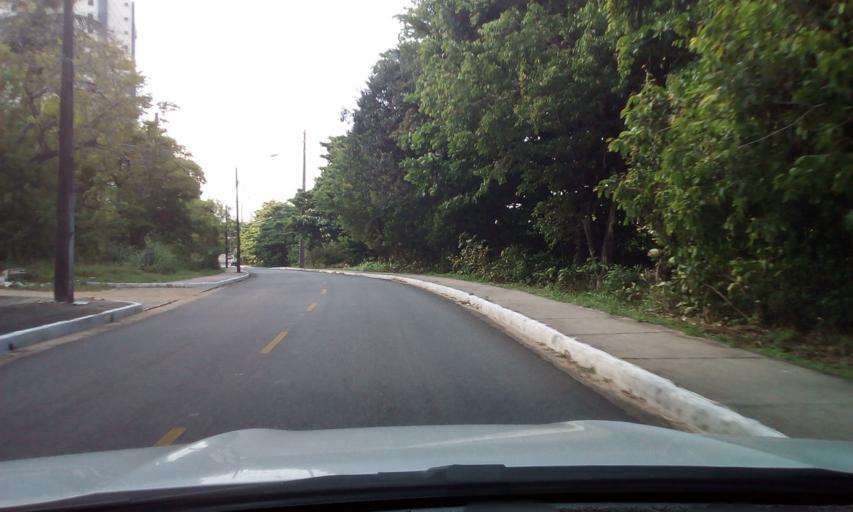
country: BR
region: Paraiba
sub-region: Joao Pessoa
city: Joao Pessoa
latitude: -7.1225
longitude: -34.8312
